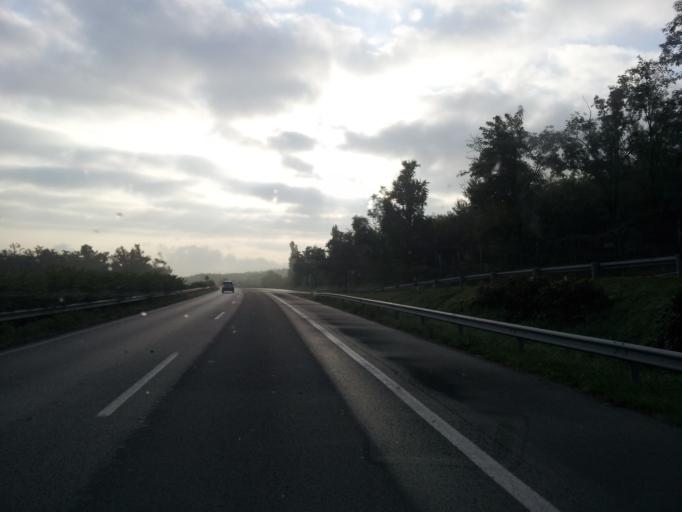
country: HU
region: Pest
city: Mogyorod
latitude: 47.6000
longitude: 19.2720
